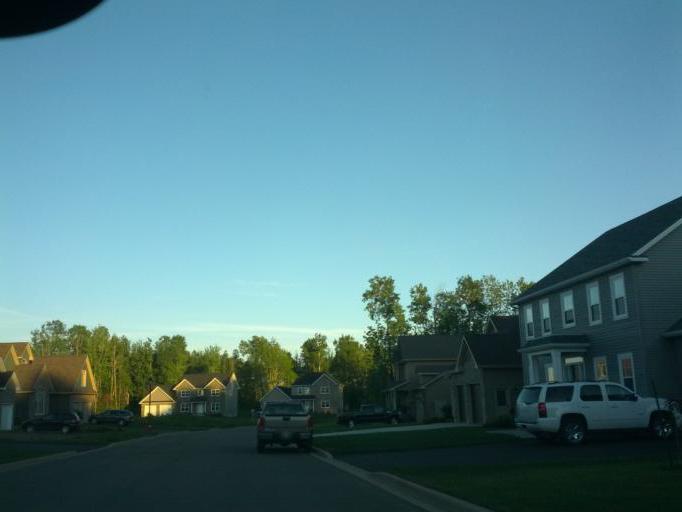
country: CA
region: New Brunswick
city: Moncton
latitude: 46.1142
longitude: -64.8692
